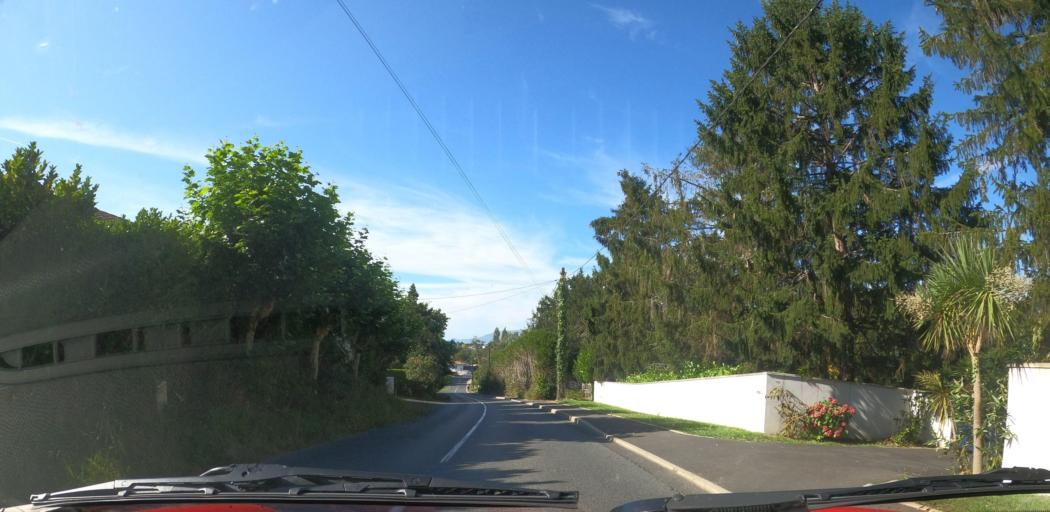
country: FR
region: Aquitaine
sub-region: Departement des Pyrenees-Atlantiques
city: Arbonne
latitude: 43.4415
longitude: -1.5464
